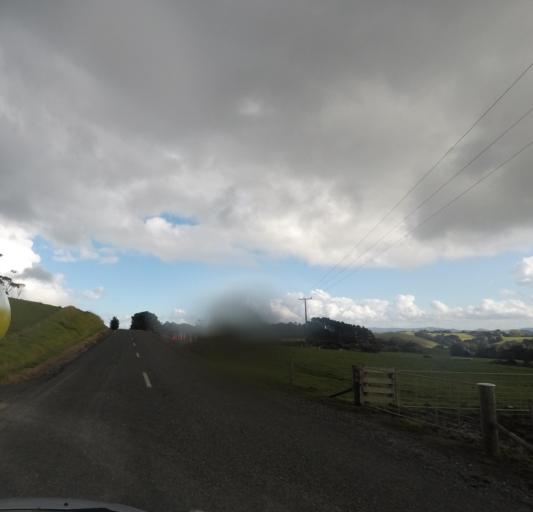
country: NZ
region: Auckland
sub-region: Auckland
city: Warkworth
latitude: -36.3707
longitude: 174.7652
